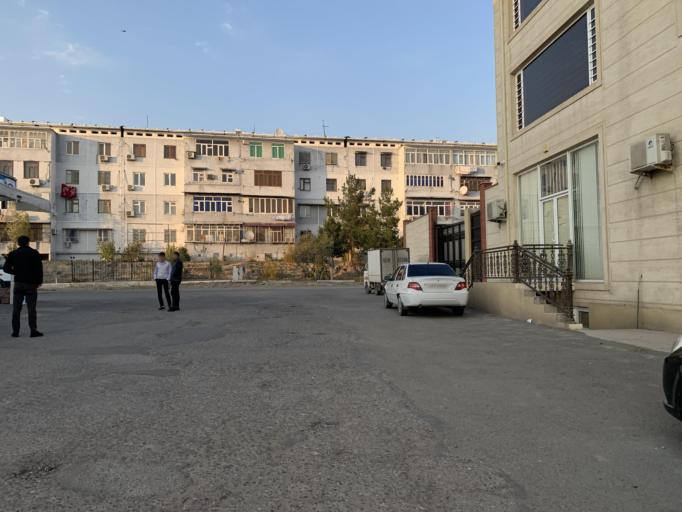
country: UZ
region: Namangan
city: Namangan Shahri
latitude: 41.0024
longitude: 71.6071
